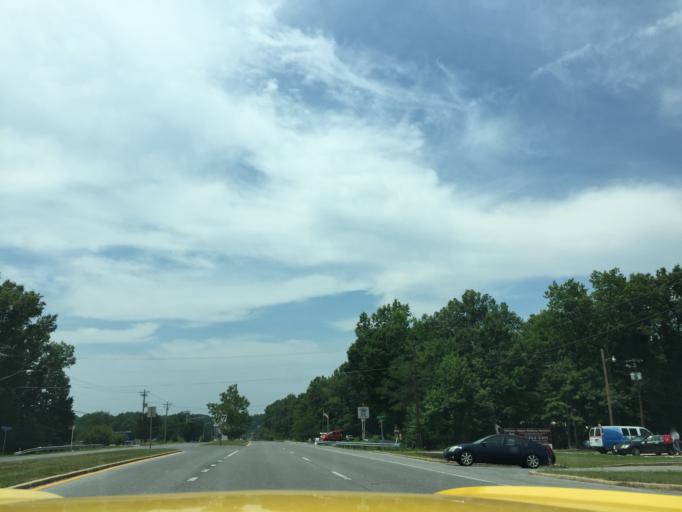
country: US
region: Maryland
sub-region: Charles County
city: Potomac Heights
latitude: 38.6012
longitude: -77.1487
